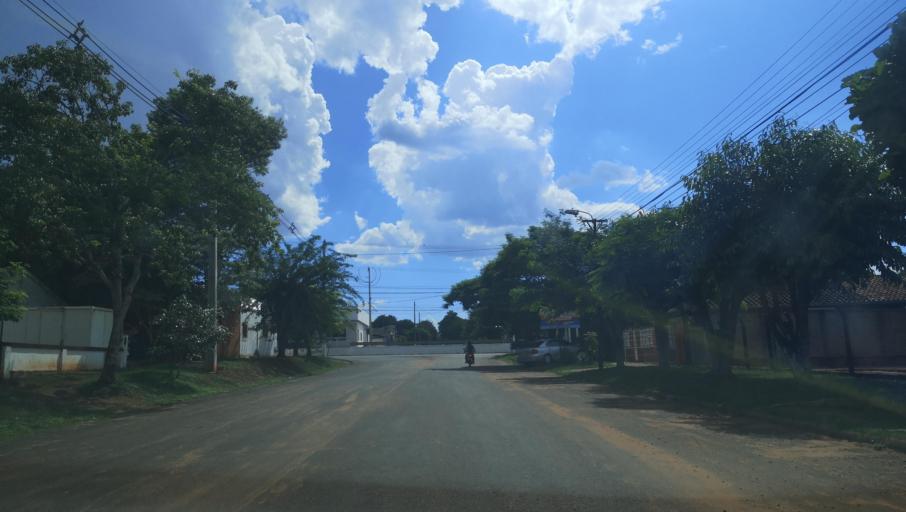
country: PY
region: Misiones
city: Santa Maria
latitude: -26.8834
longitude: -57.0311
